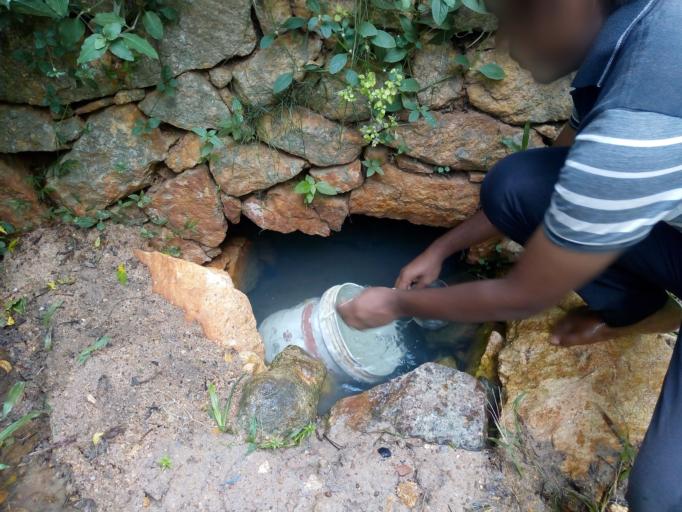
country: IN
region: Tamil Nadu
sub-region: Kanniyakumari
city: Eraniel
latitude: 8.2155
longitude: 77.2908
